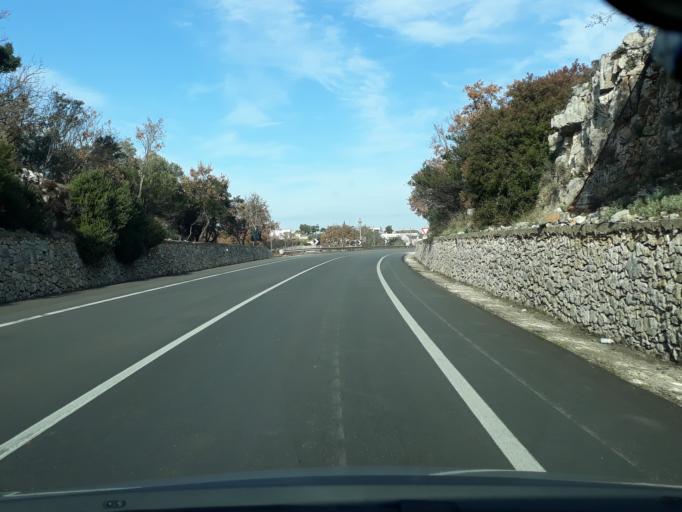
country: IT
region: Apulia
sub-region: Provincia di Bari
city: Locorotondo
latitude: 40.7828
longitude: 17.3392
